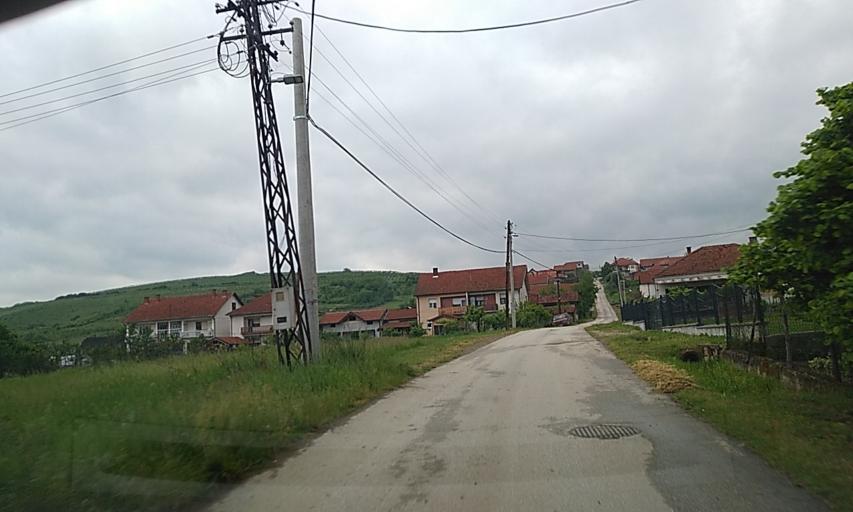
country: RS
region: Central Serbia
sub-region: Pcinjski Okrug
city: Vladicin Han
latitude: 42.7108
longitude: 22.0862
